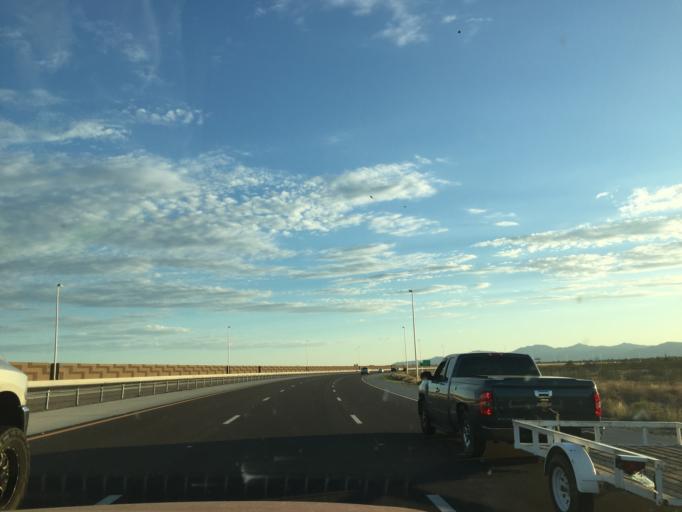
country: US
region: Arizona
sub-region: Maricopa County
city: Sun City West
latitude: 33.7026
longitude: -112.3162
